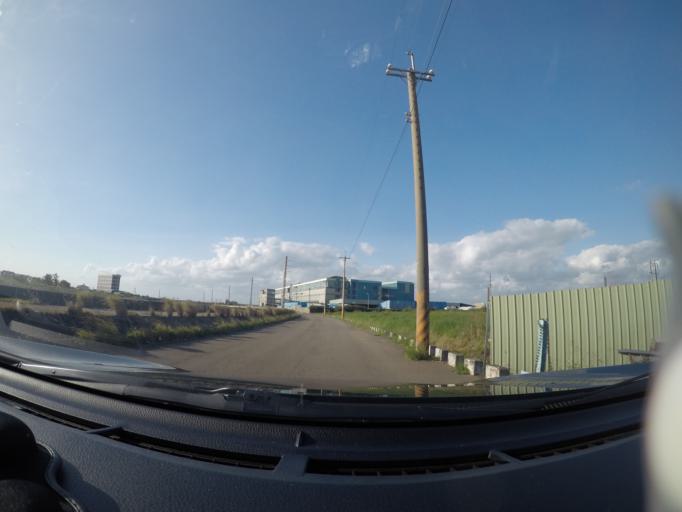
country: TW
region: Taiwan
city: Taoyuan City
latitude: 25.1059
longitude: 121.2518
